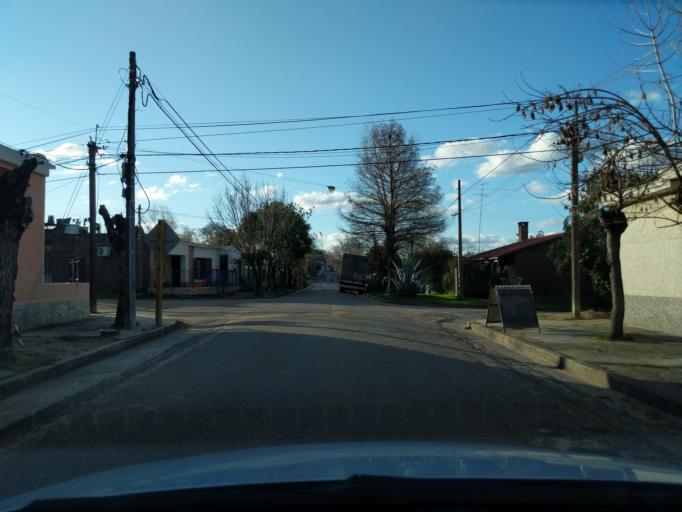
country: UY
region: Florida
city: Florida
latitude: -34.1013
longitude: -56.2251
